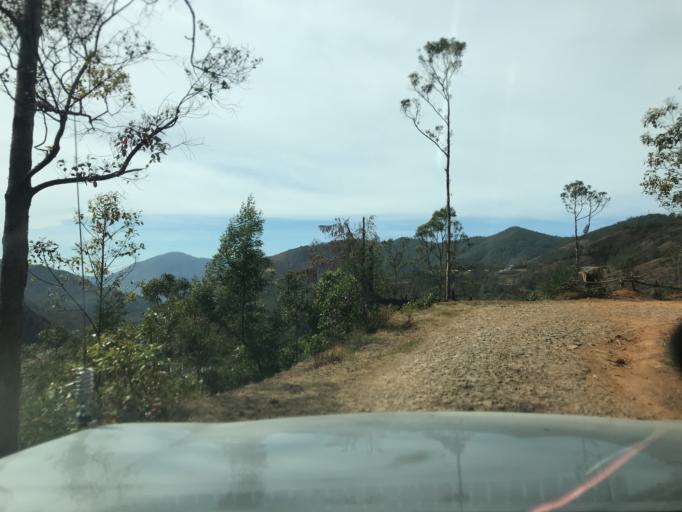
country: TL
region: Ainaro
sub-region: Ainaro
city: Ainaro
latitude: -8.8830
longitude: 125.5388
